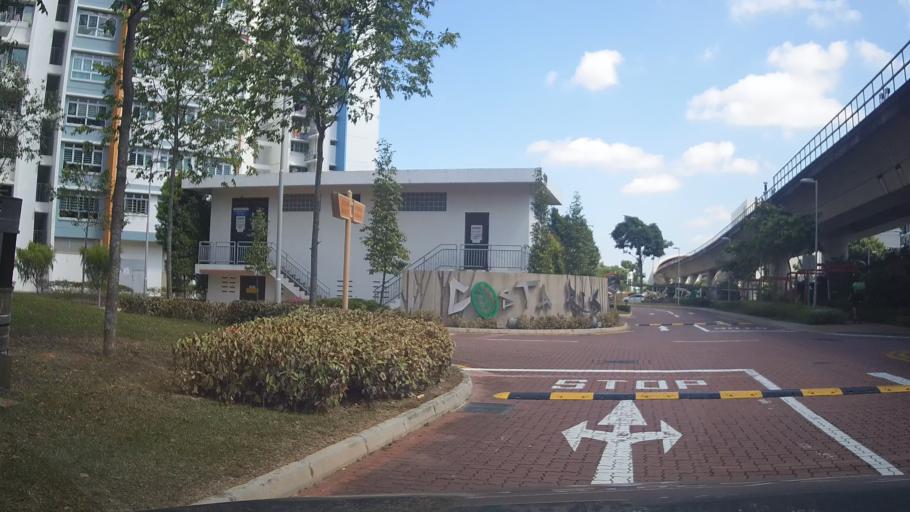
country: MY
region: Johor
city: Kampung Pasir Gudang Baru
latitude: 1.3701
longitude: 103.9483
